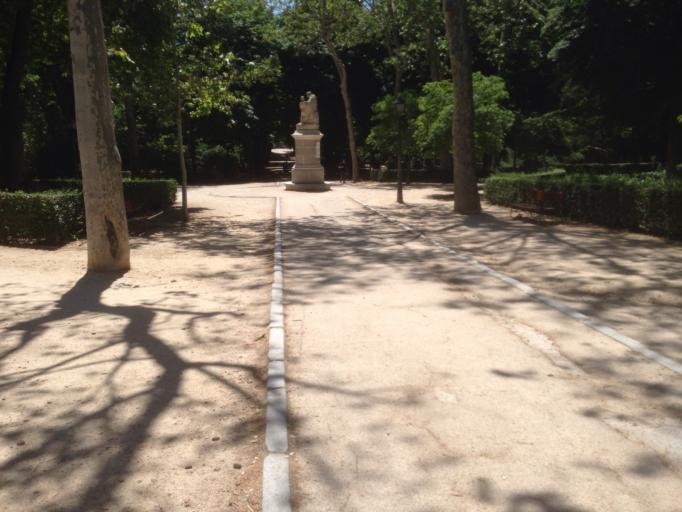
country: ES
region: Madrid
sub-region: Provincia de Madrid
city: Retiro
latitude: 40.4204
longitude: -3.6816
